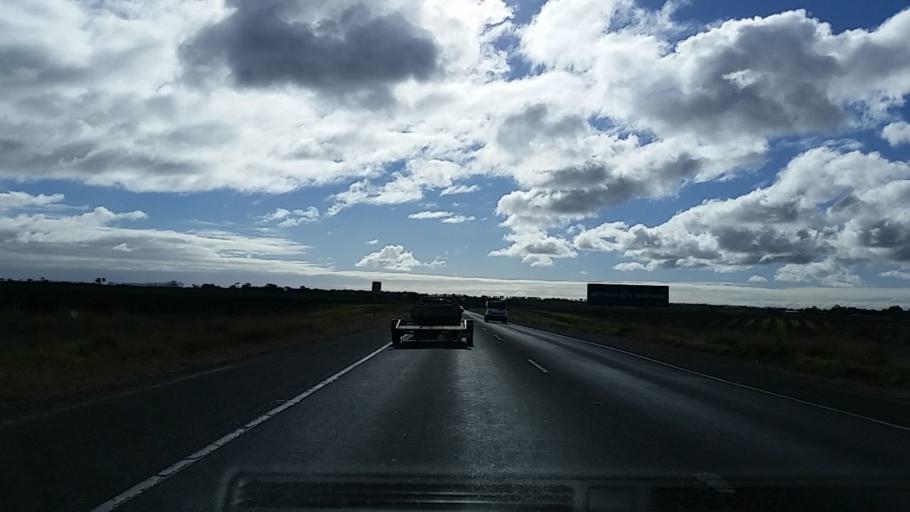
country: AU
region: South Australia
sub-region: Onkaparinga
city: McLaren Vale
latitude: -35.2615
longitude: 138.5325
